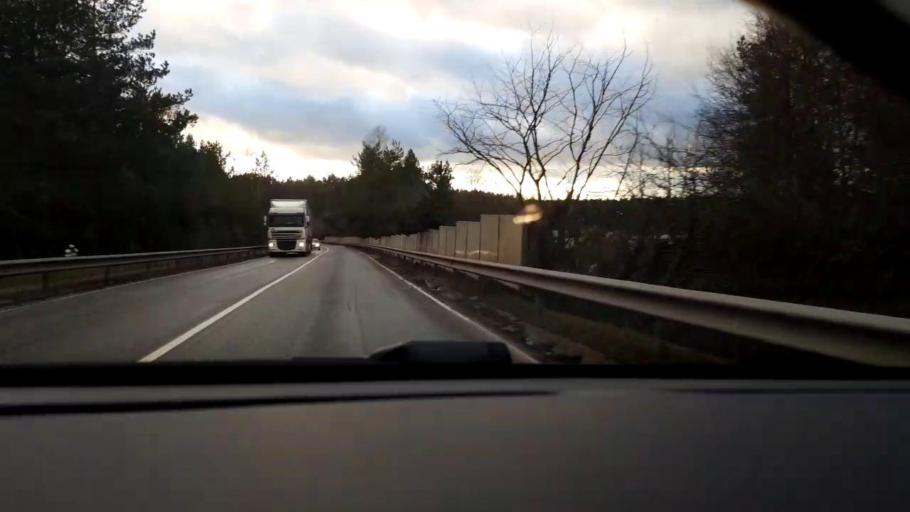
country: LT
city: Nemencine
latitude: 54.7894
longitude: 25.3859
